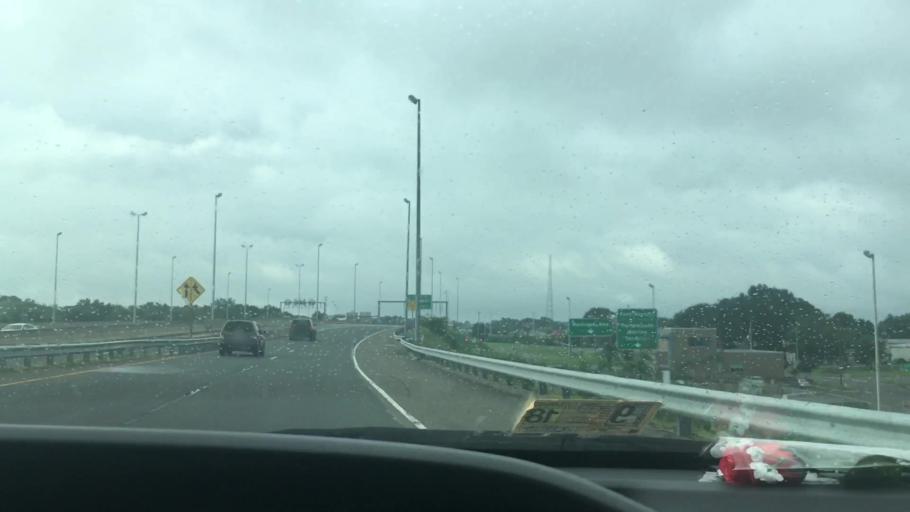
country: US
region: Virginia
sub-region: City of Portsmouth
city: Portsmouth
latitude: 36.8486
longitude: -76.3297
